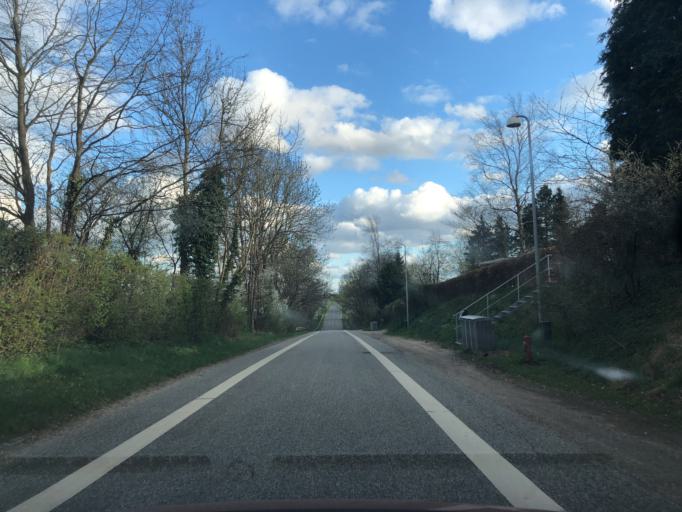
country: DK
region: Zealand
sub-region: Lejre Kommune
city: Kirke Hvalso
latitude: 55.5132
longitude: 11.8671
